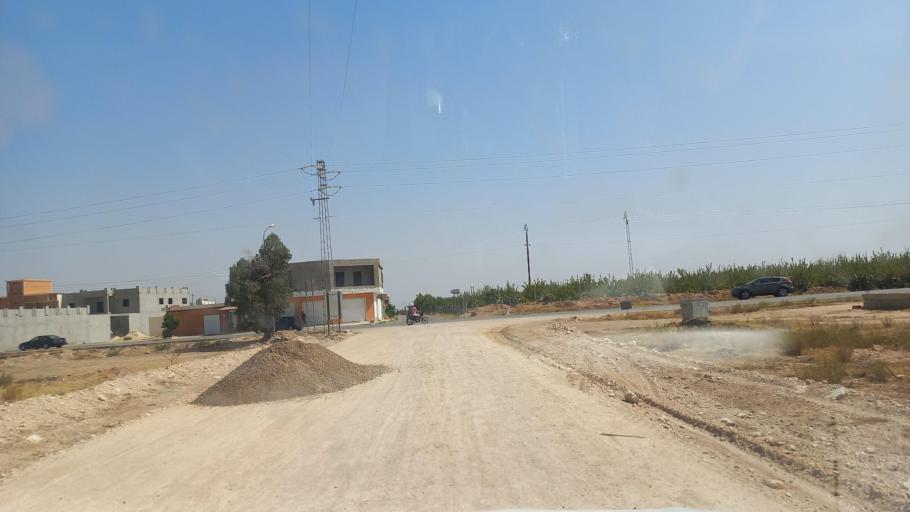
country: TN
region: Al Qasrayn
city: Kasserine
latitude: 35.2543
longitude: 9.0163
